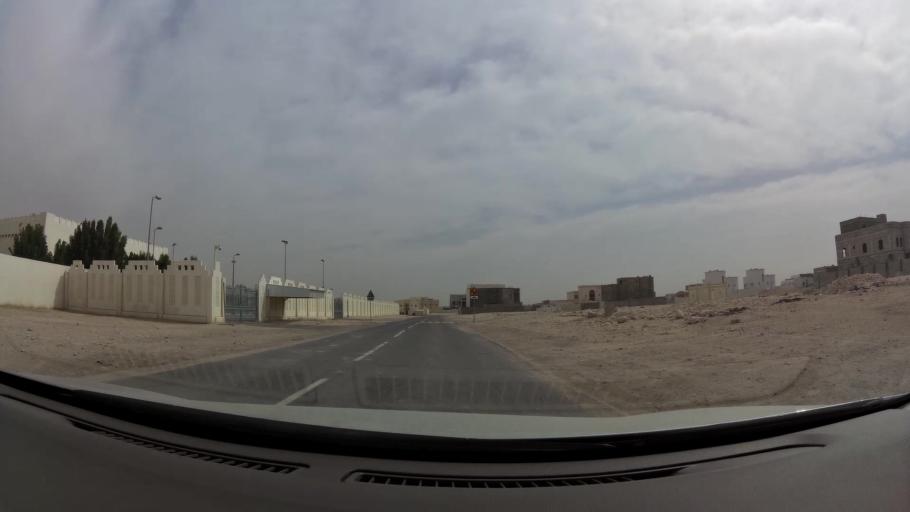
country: QA
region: Baladiyat ad Dawhah
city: Doha
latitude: 25.2161
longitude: 51.4828
